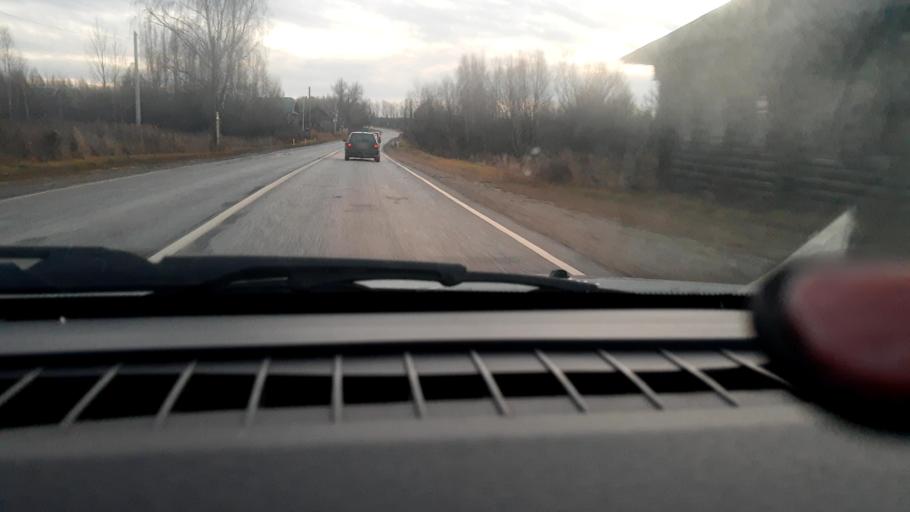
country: RU
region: Nizjnij Novgorod
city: Krasnyye Baki
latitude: 57.0145
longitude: 45.1153
